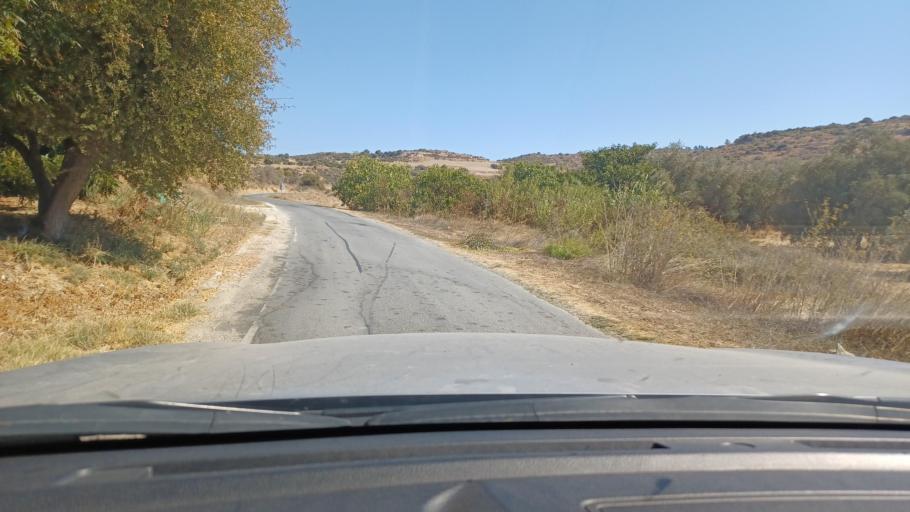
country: CY
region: Pafos
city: Polis
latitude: 35.0277
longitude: 32.4571
